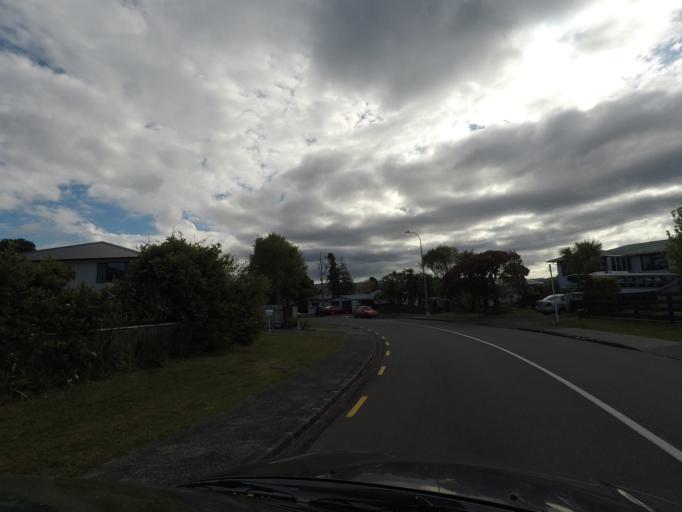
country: NZ
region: Auckland
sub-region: Auckland
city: Rosebank
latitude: -36.8679
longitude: 174.6428
